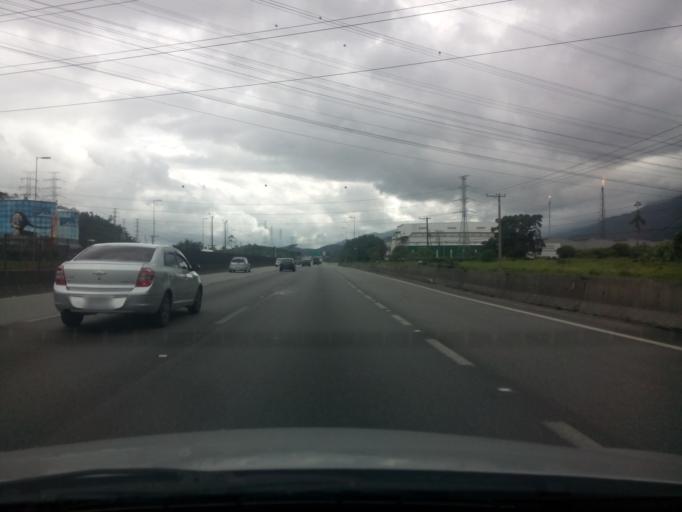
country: BR
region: Sao Paulo
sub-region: Cubatao
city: Cubatao
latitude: -23.8602
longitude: -46.4129
